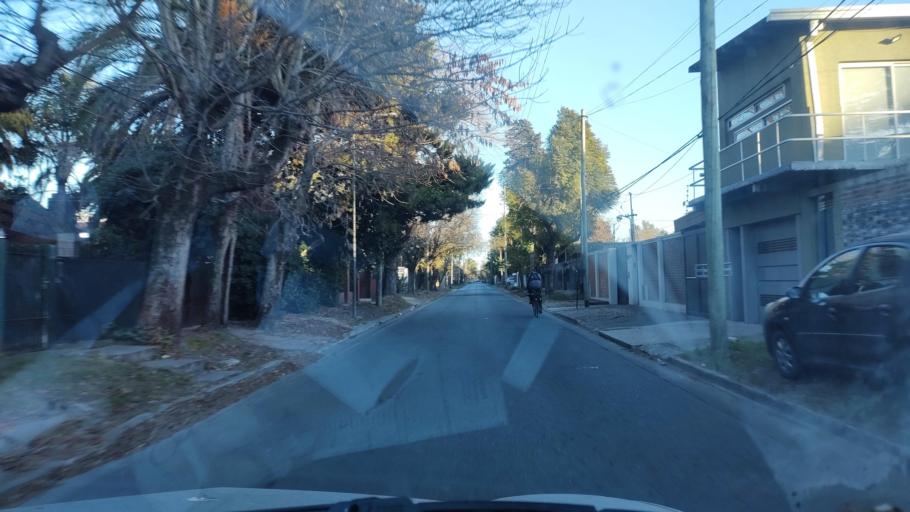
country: AR
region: Buenos Aires
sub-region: Partido de La Plata
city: La Plata
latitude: -34.8902
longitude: -58.0295
